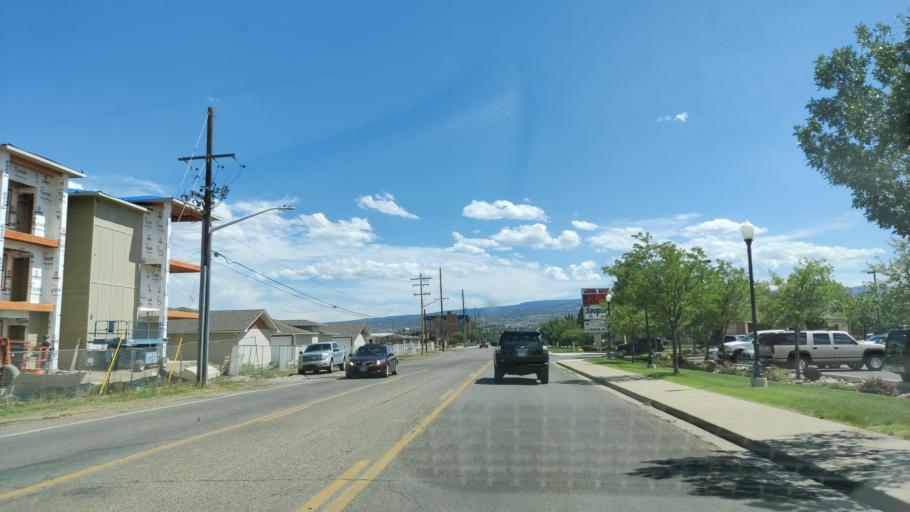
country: US
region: Colorado
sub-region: Mesa County
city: Redlands
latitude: 39.0953
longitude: -108.5989
